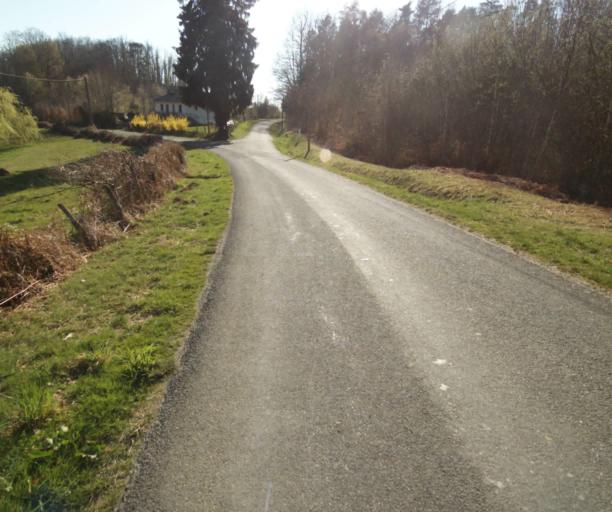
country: FR
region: Limousin
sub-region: Departement de la Correze
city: Saint-Mexant
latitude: 45.3141
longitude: 1.6139
